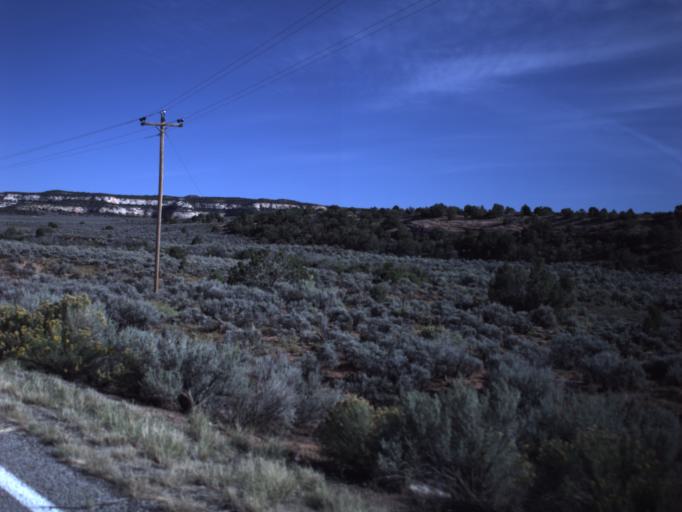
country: US
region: Utah
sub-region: Grand County
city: Moab
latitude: 38.3053
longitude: -109.3914
